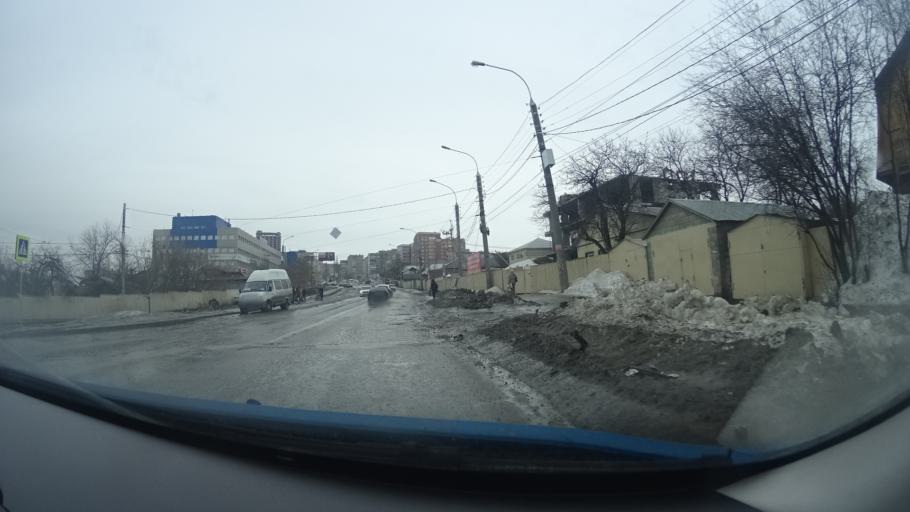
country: RU
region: Bashkortostan
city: Ufa
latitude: 54.7110
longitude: 55.9824
